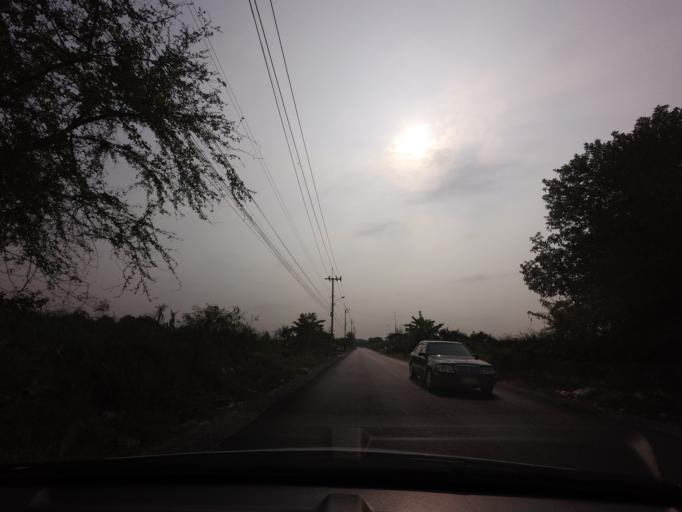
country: TH
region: Bangkok
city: Nong Khaem
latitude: 13.7357
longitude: 100.3506
